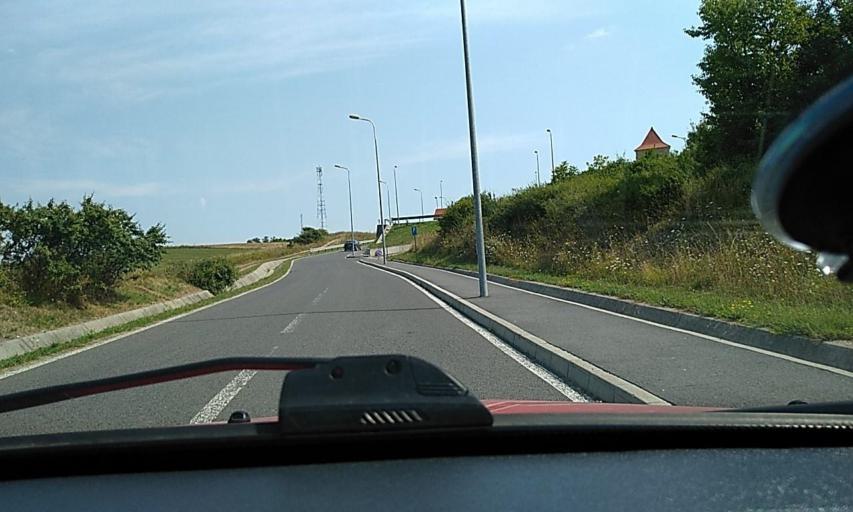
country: RO
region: Brasov
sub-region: Oras Rupea
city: Rupea
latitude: 46.0375
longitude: 25.2108
